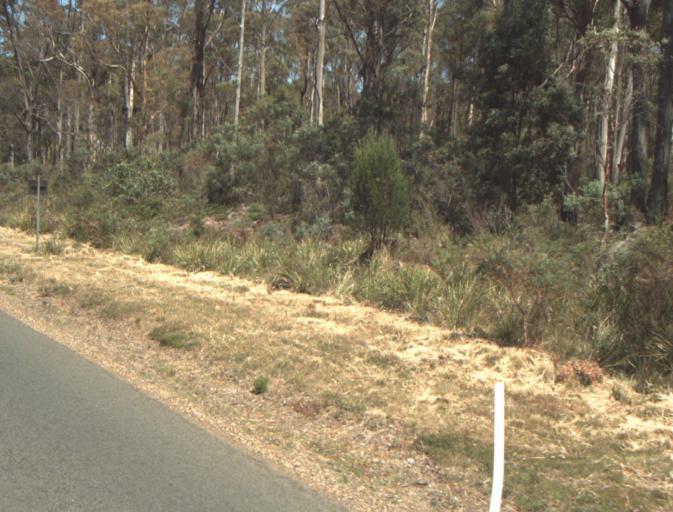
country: AU
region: Tasmania
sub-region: Launceston
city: Mayfield
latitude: -41.2902
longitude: 147.1293
